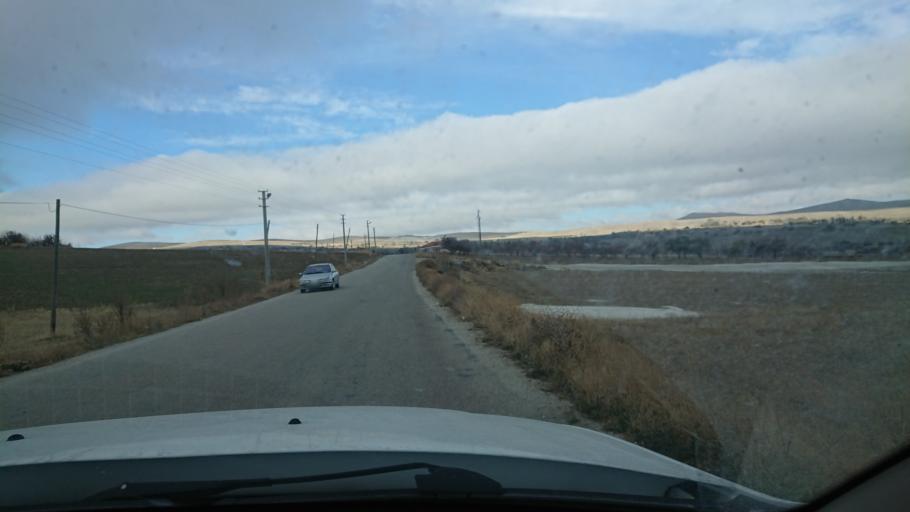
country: TR
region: Aksaray
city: Ortakoy
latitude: 38.7491
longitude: 34.0267
